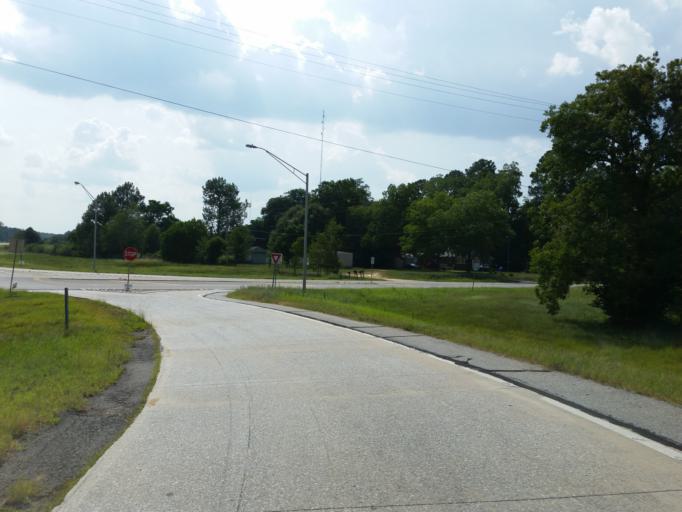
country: US
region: Georgia
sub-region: Crisp County
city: Cordele
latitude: 31.9239
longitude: -83.7713
